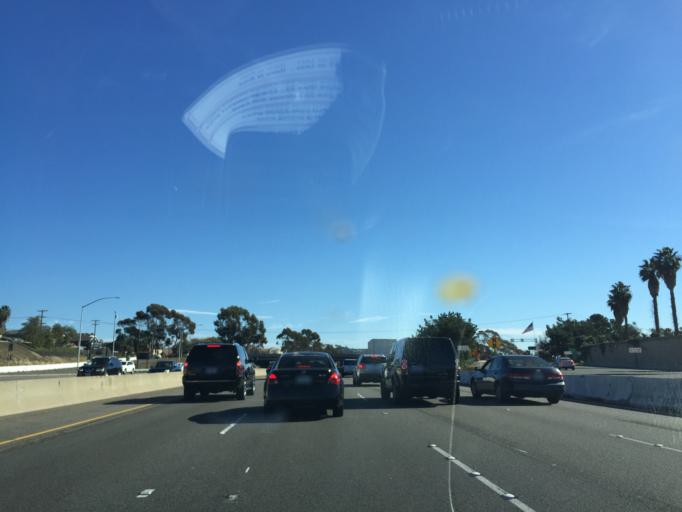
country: US
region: California
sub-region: Orange County
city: Dana Point
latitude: 33.4600
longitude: -117.6585
